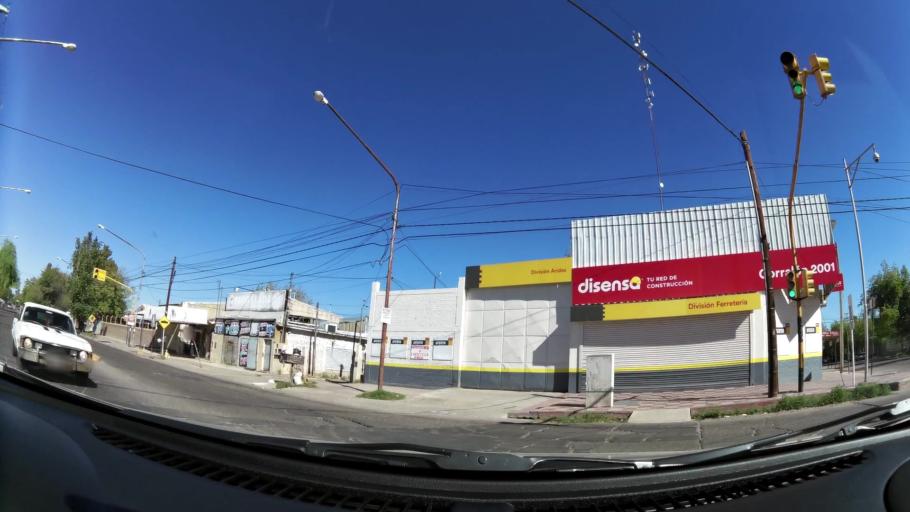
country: AR
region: Mendoza
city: Las Heras
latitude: -32.8423
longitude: -68.8118
